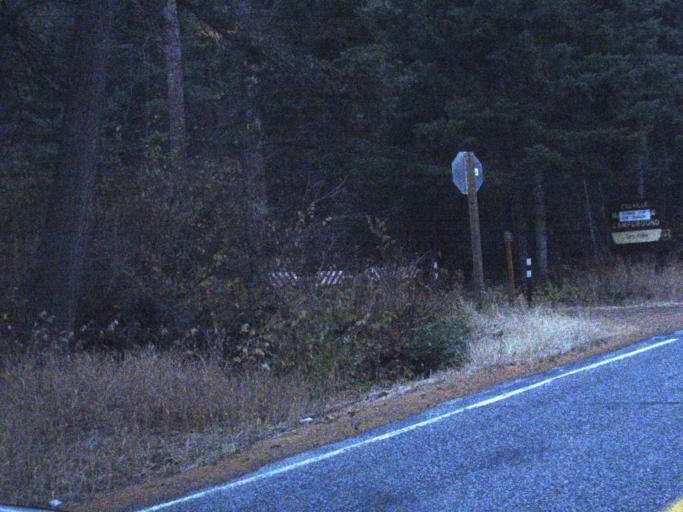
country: US
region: Washington
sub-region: Ferry County
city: Republic
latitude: 48.5179
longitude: -118.7384
